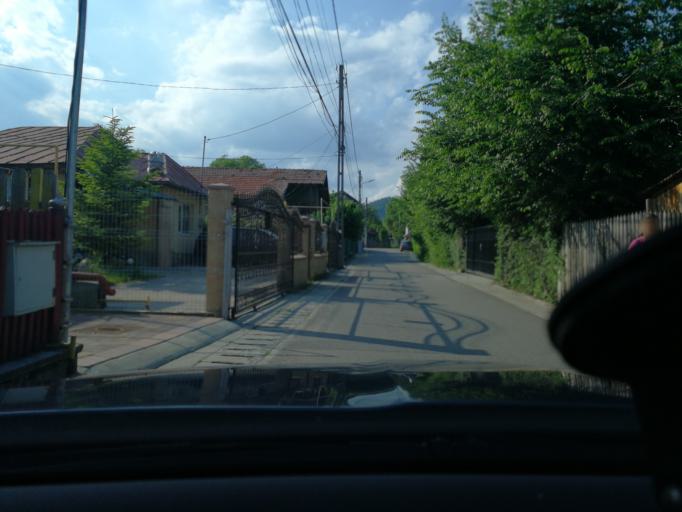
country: RO
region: Prahova
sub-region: Comuna Cornu
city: Cornu de Jos
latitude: 45.1596
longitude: 25.7017
